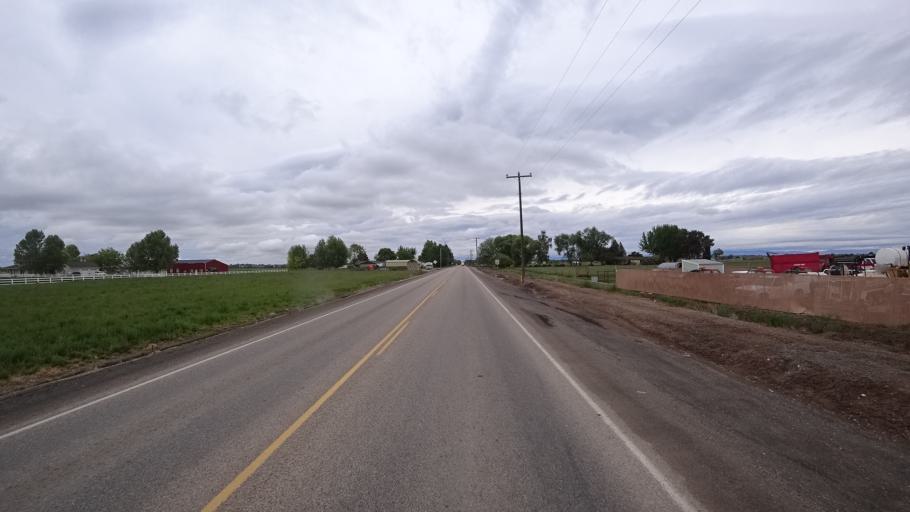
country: US
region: Idaho
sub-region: Ada County
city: Star
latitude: 43.6337
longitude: -116.4935
